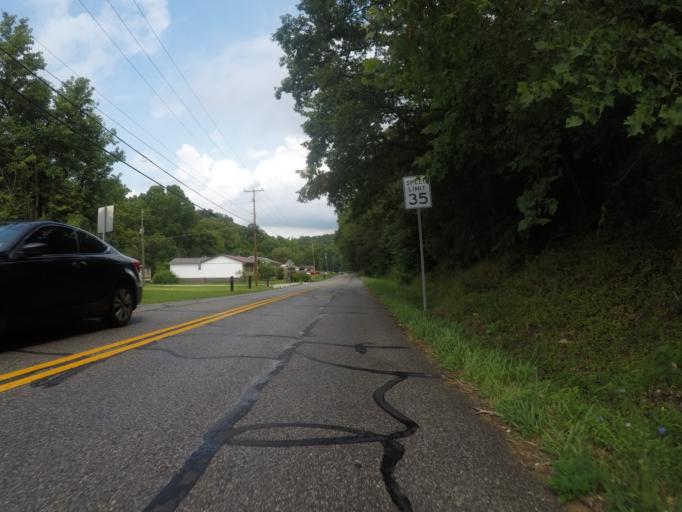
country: US
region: Kentucky
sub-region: Boyd County
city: Meads
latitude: 38.4135
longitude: -82.6807
